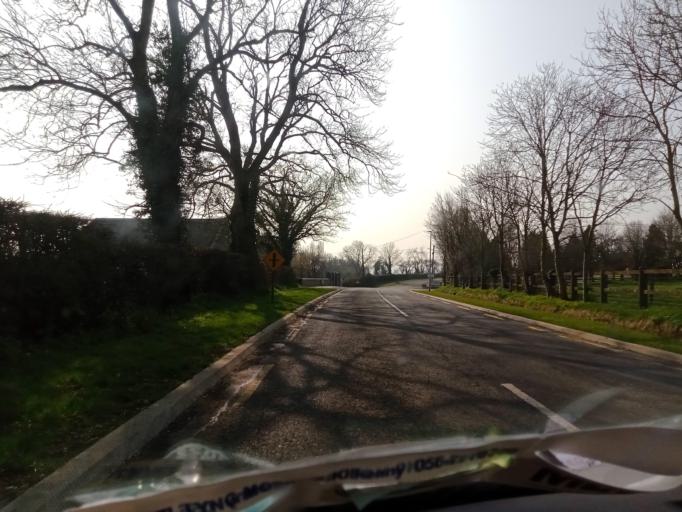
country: IE
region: Leinster
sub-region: Kilkenny
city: Callan
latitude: 52.5007
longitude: -7.3814
